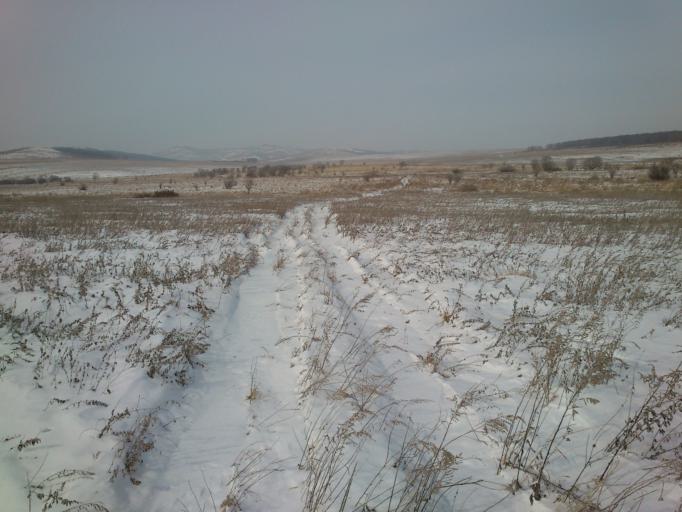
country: RU
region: Primorskiy
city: Sergeyevka
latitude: 44.3699
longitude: 131.8488
